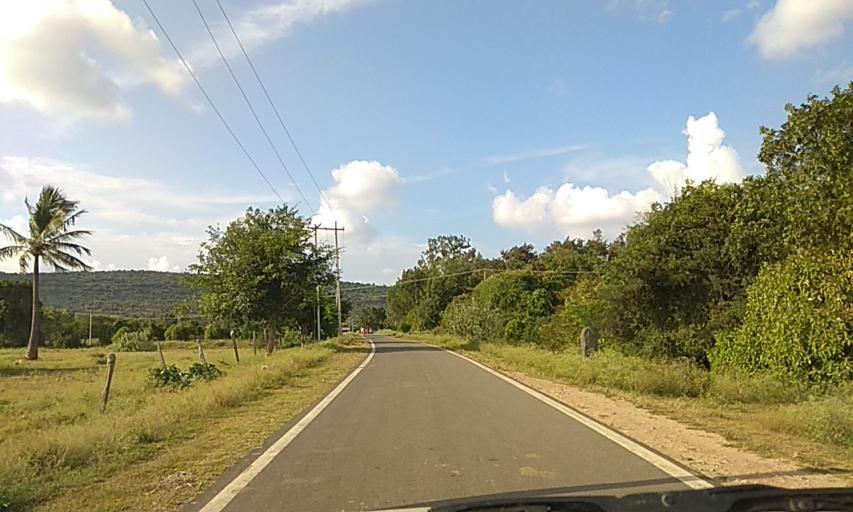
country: IN
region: Karnataka
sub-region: Chamrajnagar
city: Gundlupet
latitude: 11.7692
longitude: 76.7831
